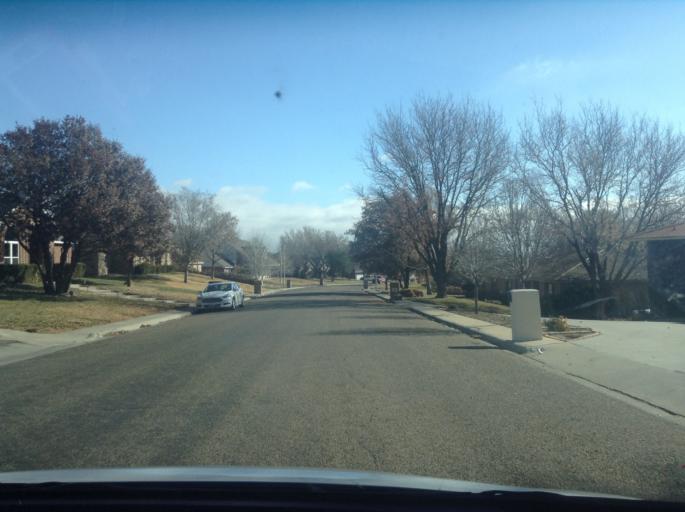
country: US
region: Texas
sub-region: Randall County
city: Canyon
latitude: 34.9957
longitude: -101.9286
